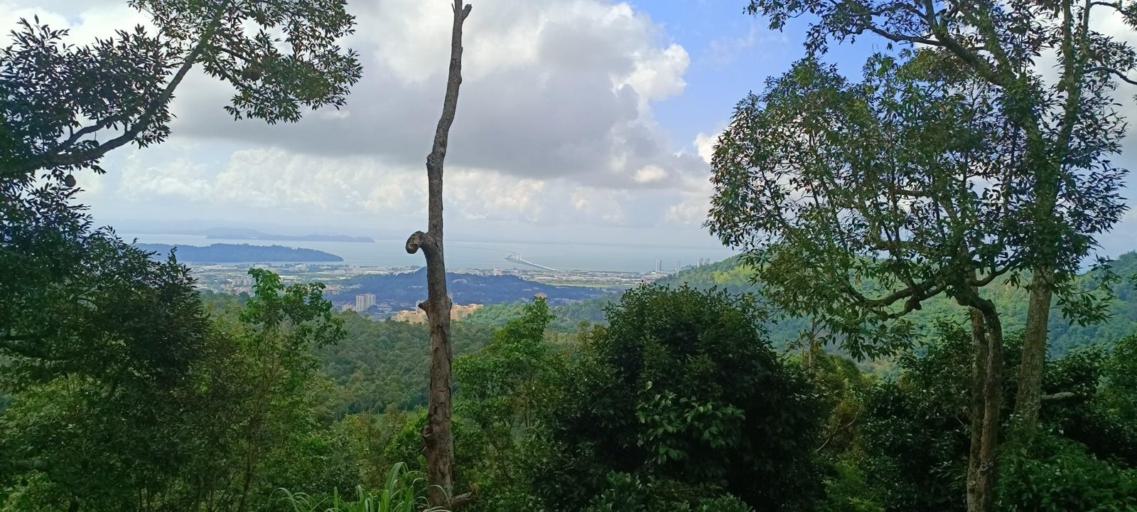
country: MY
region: Penang
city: Kampung Sungai Ara
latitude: 5.3324
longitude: 100.2480
